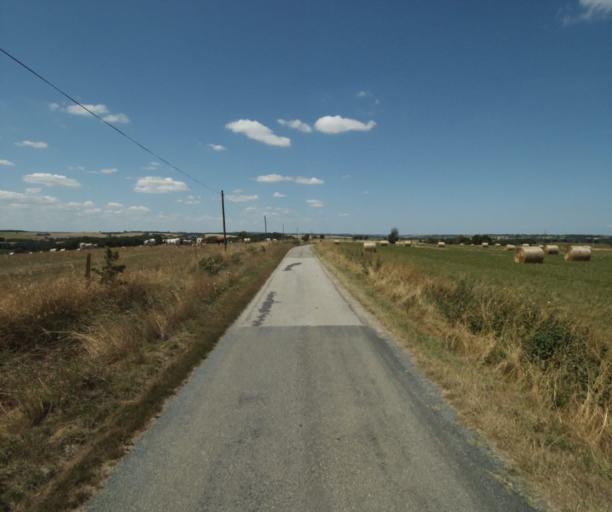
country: FR
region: Midi-Pyrenees
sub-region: Departement de la Haute-Garonne
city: Saint-Felix-Lauragais
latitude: 43.4837
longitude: 1.8637
